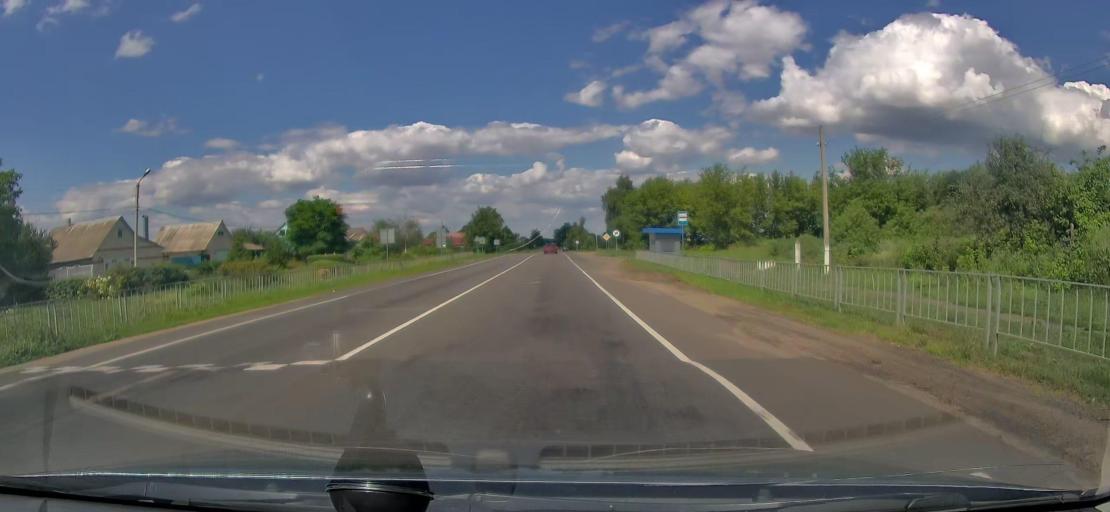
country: RU
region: Kursk
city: Zolotukhino
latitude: 51.9147
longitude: 36.3057
